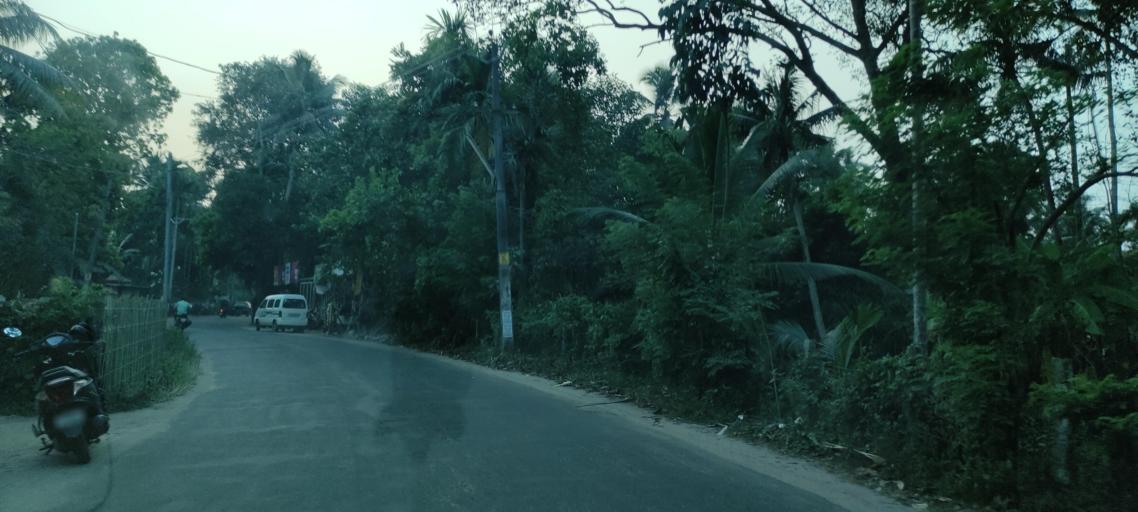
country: IN
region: Kerala
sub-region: Alappuzha
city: Kayankulam
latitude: 9.1212
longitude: 76.4944
